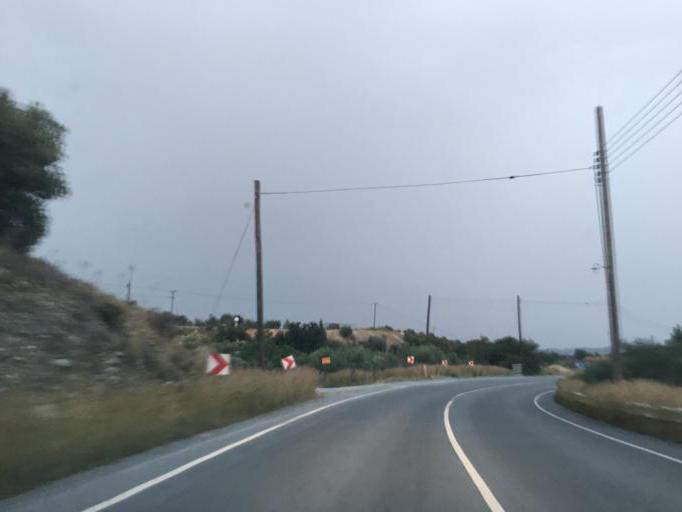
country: CY
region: Limassol
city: Parekklisha
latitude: 34.7727
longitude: 33.1623
